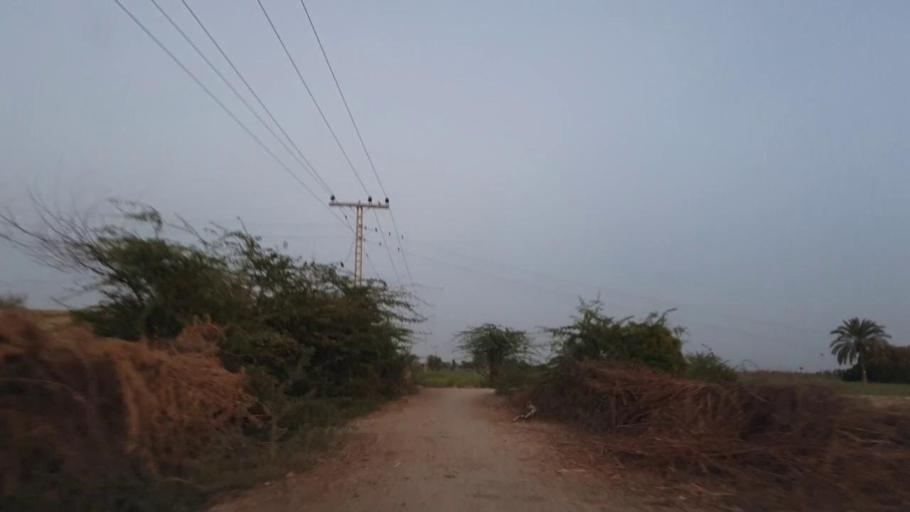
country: PK
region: Sindh
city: Pithoro
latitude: 25.3998
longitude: 69.2661
